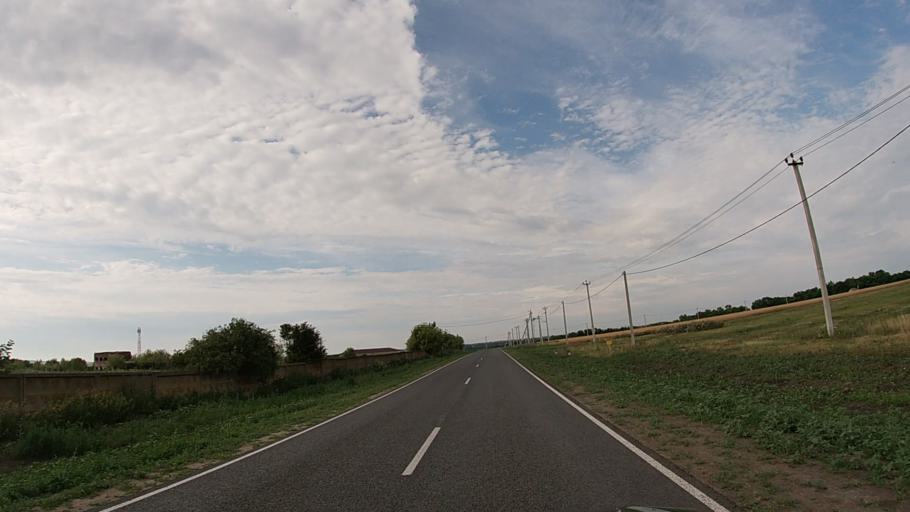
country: RU
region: Belgorod
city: Severnyy
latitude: 50.7239
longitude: 36.5844
